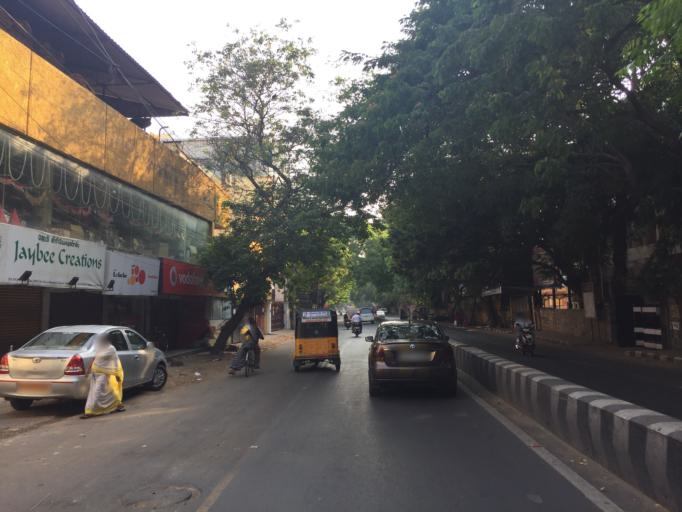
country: IN
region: Tamil Nadu
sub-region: Chennai
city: Gandhi Nagar
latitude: 13.0233
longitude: 80.2641
